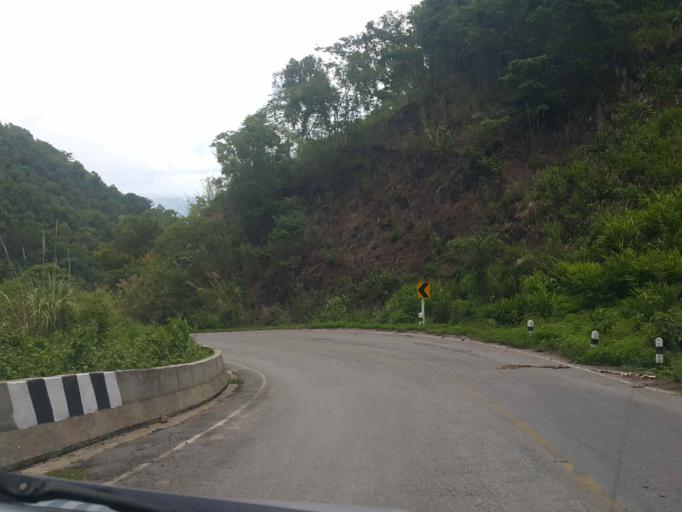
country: TH
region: Phayao
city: Chiang Muan
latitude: 18.9214
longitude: 100.1945
